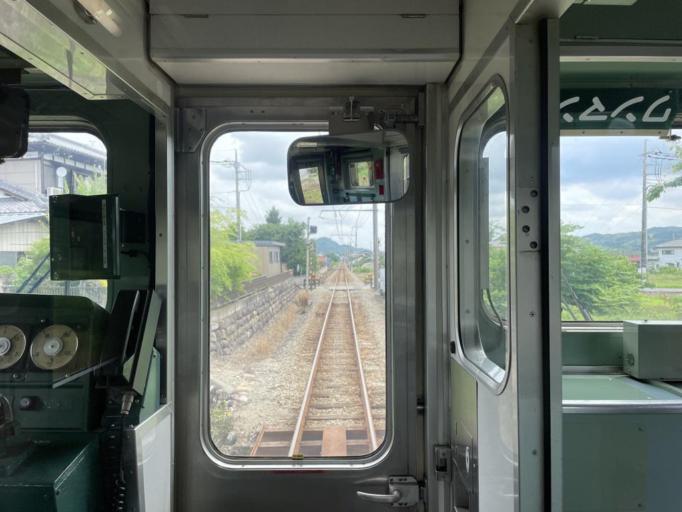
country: JP
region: Gunma
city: Tomioka
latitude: 36.2340
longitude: 138.8056
